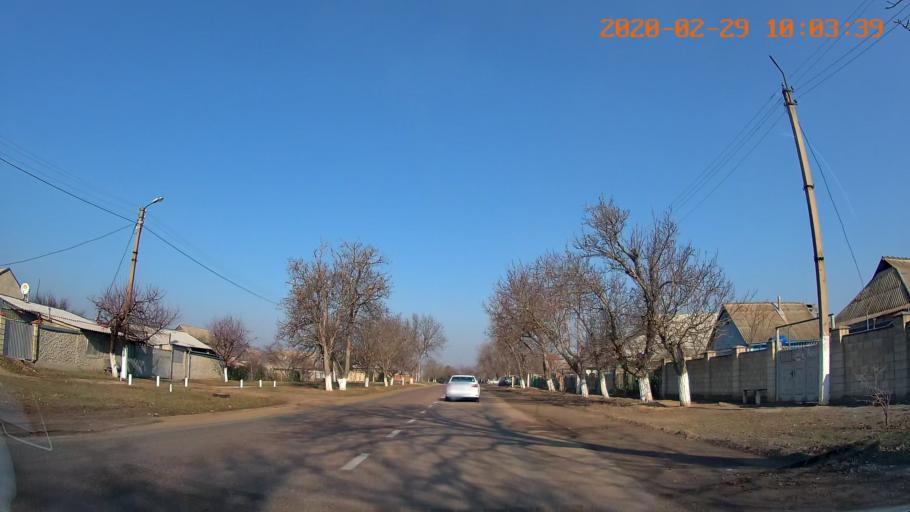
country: MD
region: Causeni
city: Chitcani
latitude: 46.7922
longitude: 29.6794
